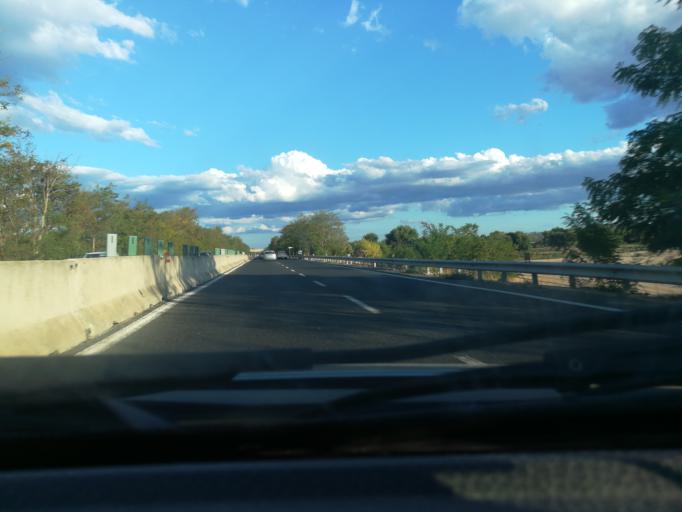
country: IT
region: Apulia
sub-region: Provincia di Bari
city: Mola di Bari
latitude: 41.0397
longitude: 17.1189
